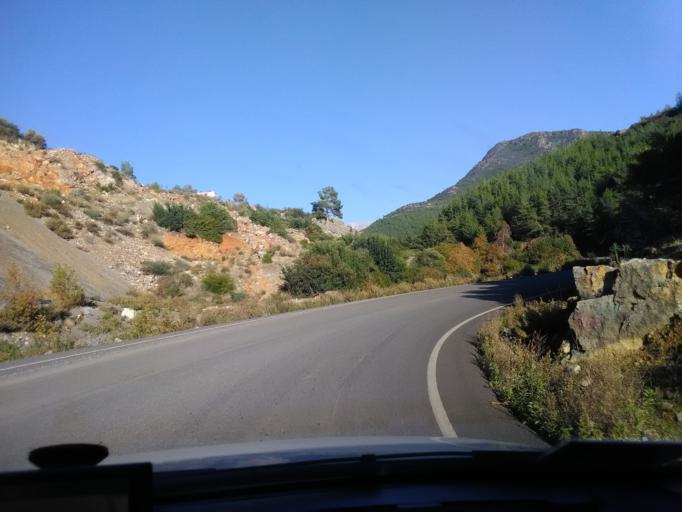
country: TR
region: Antalya
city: Gazipasa
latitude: 36.2823
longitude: 32.3638
